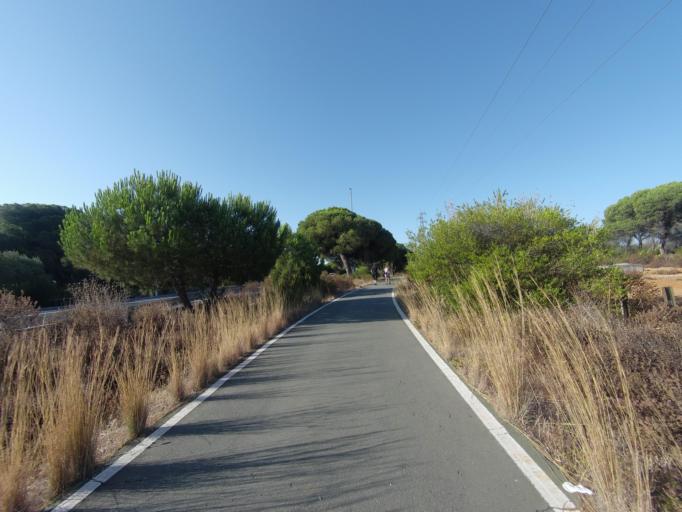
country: ES
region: Andalusia
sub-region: Provincia de Huelva
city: Aljaraque
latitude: 37.2140
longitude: -7.0269
